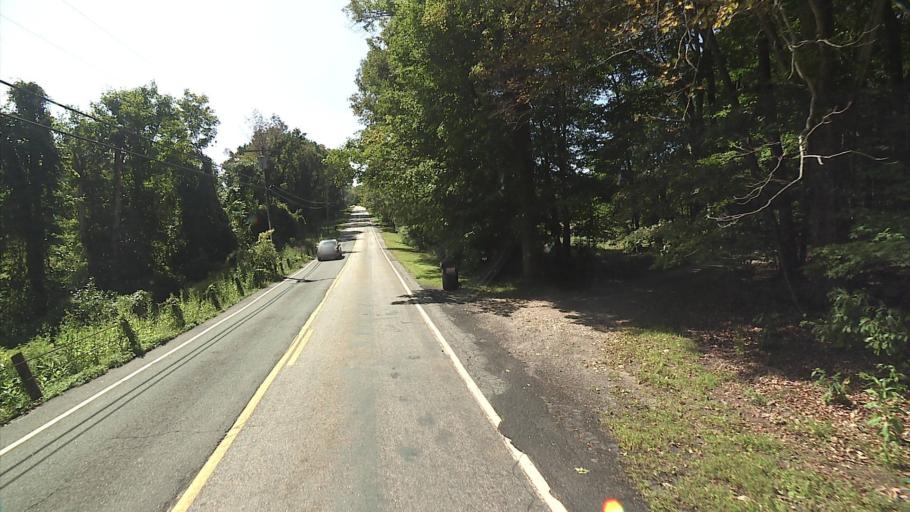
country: US
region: Connecticut
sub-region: Litchfield County
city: Northwest Harwinton
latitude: 41.7309
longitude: -73.0745
